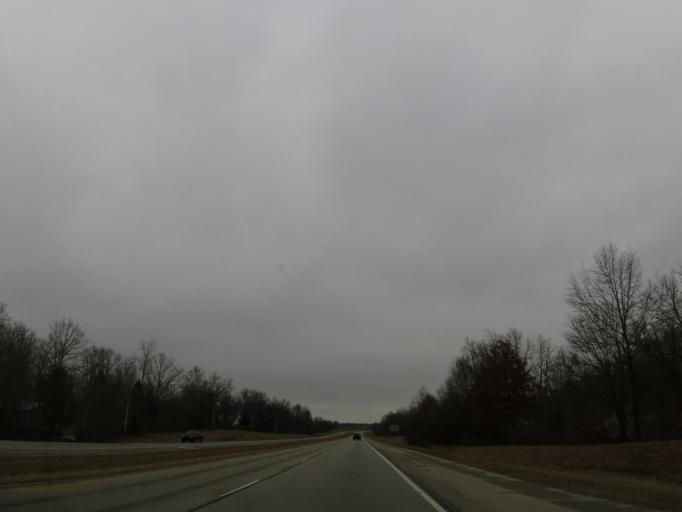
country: US
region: Kentucky
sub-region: Anderson County
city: Lawrenceburg
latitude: 38.0831
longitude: -84.9183
